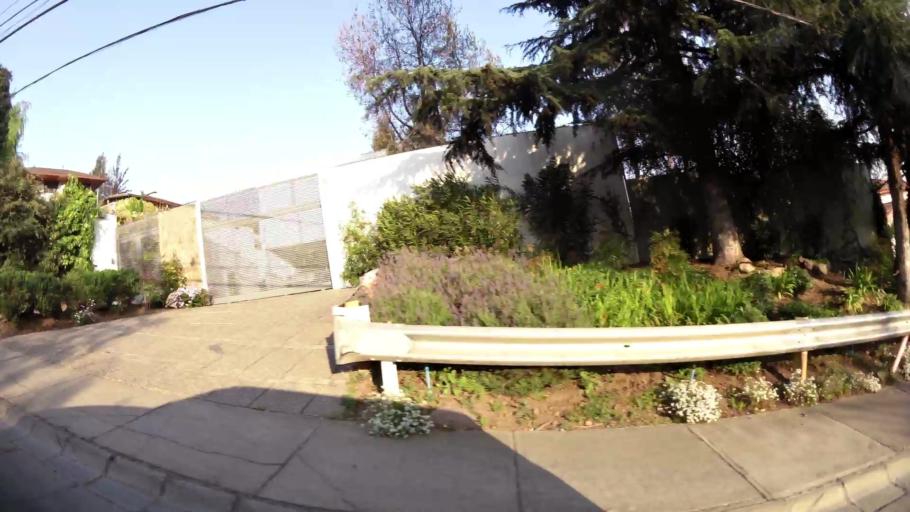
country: CL
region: Santiago Metropolitan
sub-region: Provincia de Santiago
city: Villa Presidente Frei, Nunoa, Santiago, Chile
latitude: -33.3414
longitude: -70.5097
